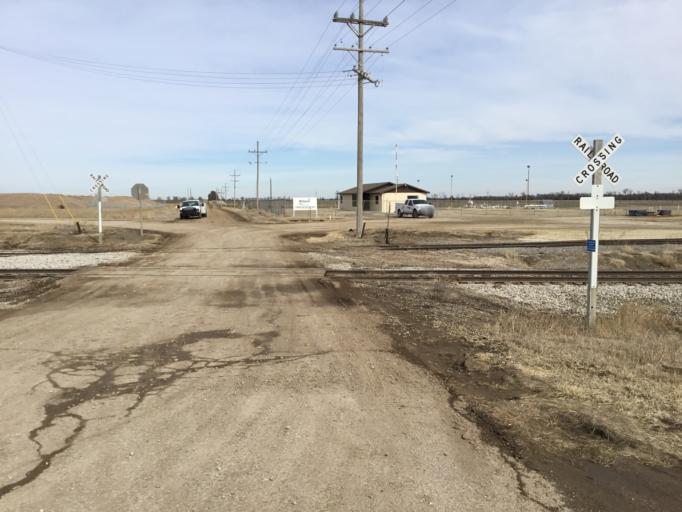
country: US
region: Kansas
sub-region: McPherson County
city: McPherson
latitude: 38.3723
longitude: -97.7958
